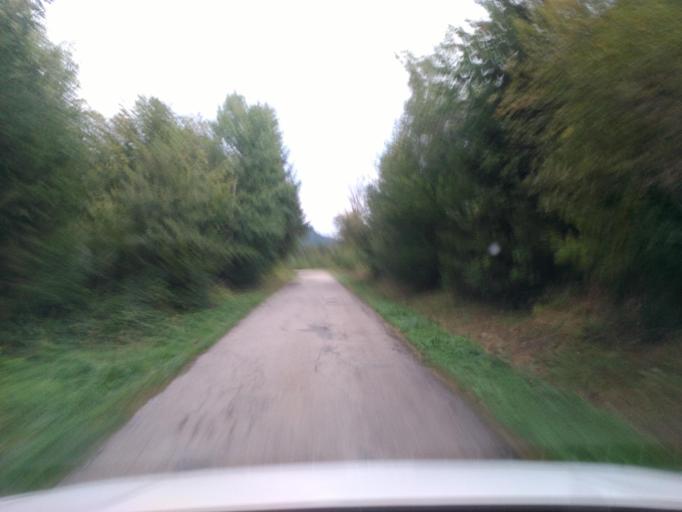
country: FR
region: Lorraine
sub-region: Departement des Vosges
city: Senones
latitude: 48.3952
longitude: 7.0374
